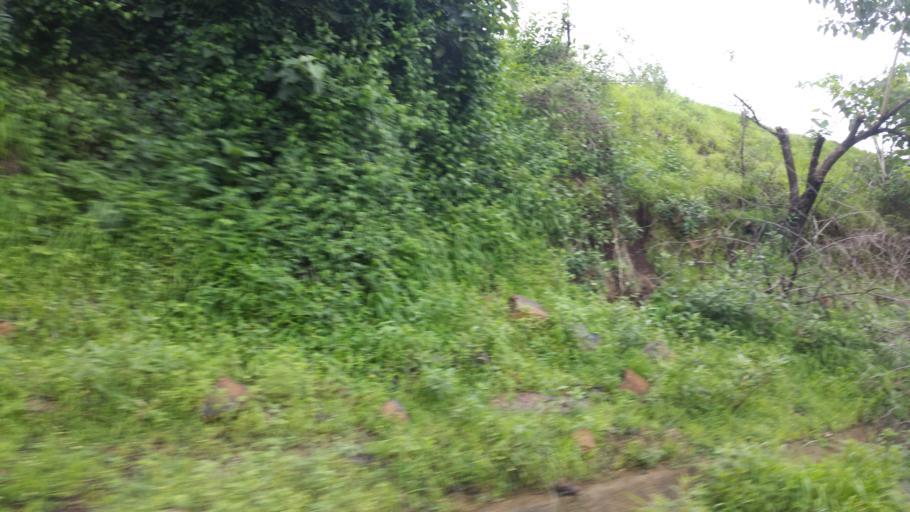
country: ET
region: Amhara
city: Debark'
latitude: 13.3822
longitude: 37.9857
